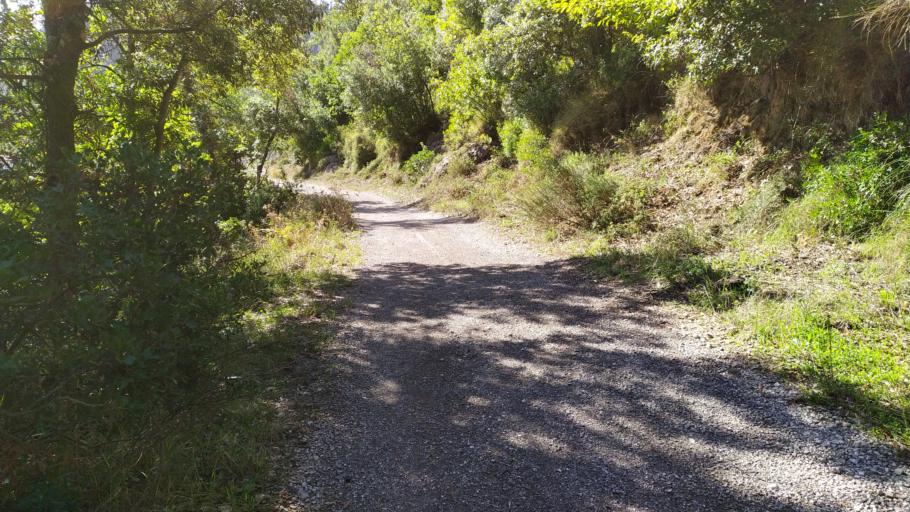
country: IT
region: Campania
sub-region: Provincia di Salerno
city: Vietri sul Mare
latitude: 40.6835
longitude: 14.7348
